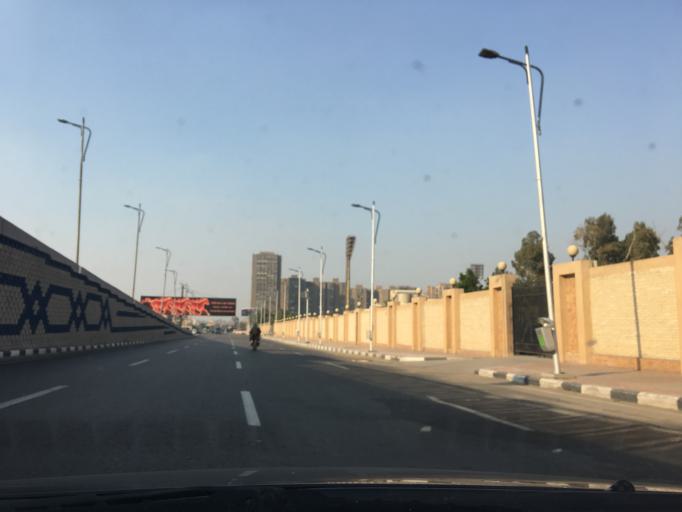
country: EG
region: Muhafazat al Qahirah
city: Cairo
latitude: 30.0681
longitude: 31.3050
